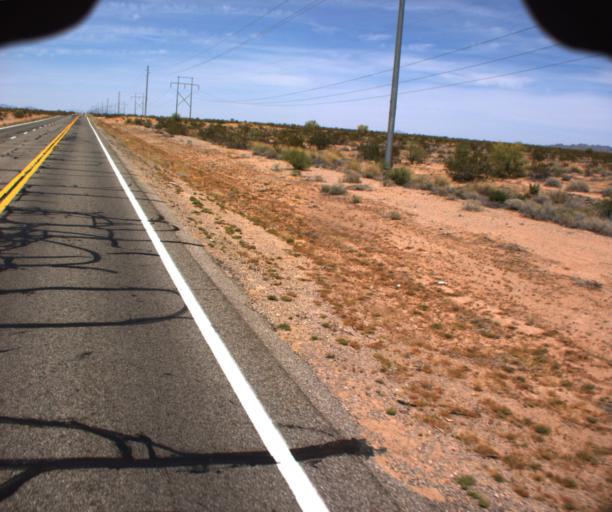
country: US
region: Arizona
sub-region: La Paz County
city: Quartzsite
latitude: 33.8060
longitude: -114.2170
